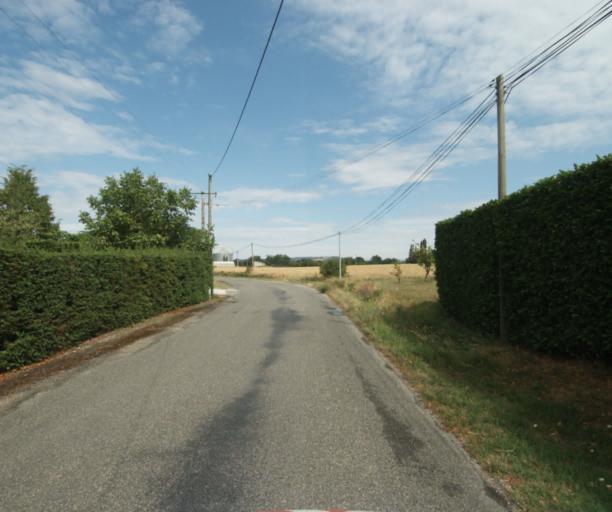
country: FR
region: Midi-Pyrenees
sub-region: Departement de la Haute-Garonne
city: Revel
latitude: 43.4485
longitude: 1.9617
